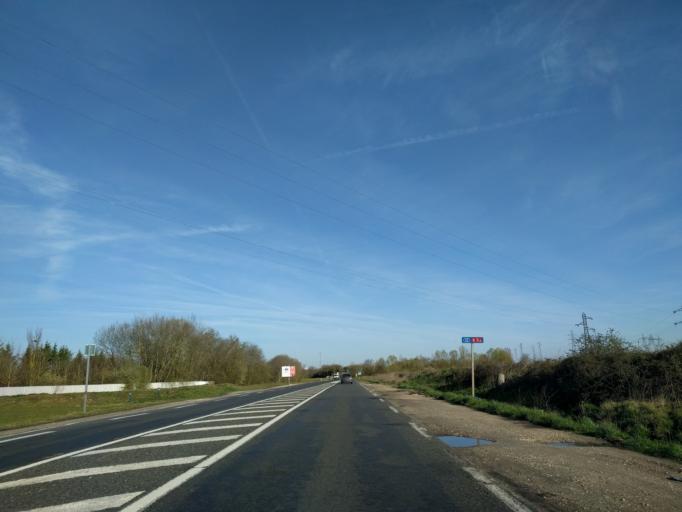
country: FR
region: Ile-de-France
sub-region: Departement de Seine-et-Marne
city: Moissy-Cramayel
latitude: 48.6036
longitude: 2.5850
